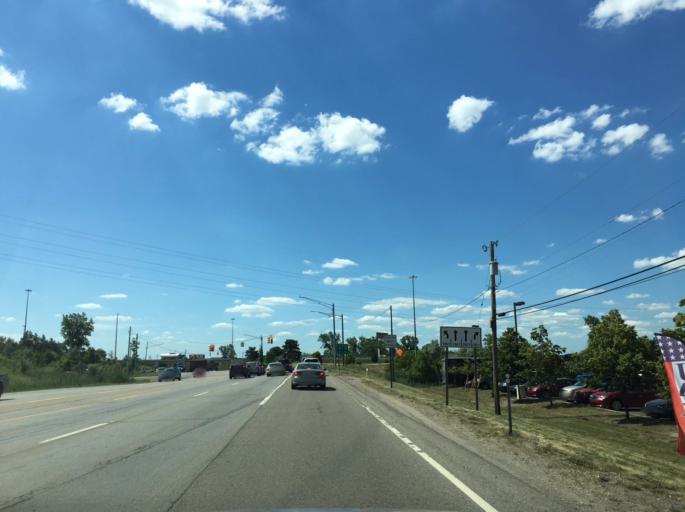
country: US
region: Michigan
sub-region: Oakland County
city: Auburn Hills
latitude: 42.7045
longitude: -83.2852
